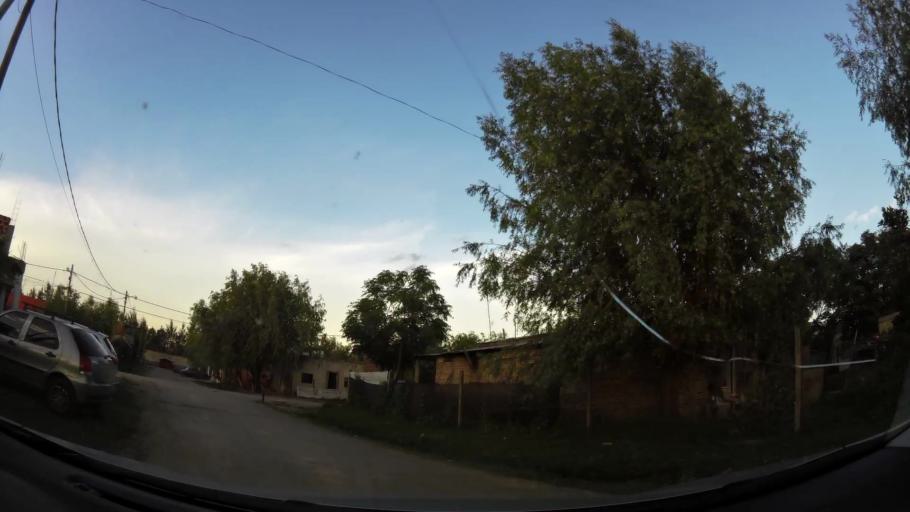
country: AR
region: Buenos Aires
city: Santa Catalina - Dique Lujan
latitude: -34.4393
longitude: -58.6615
